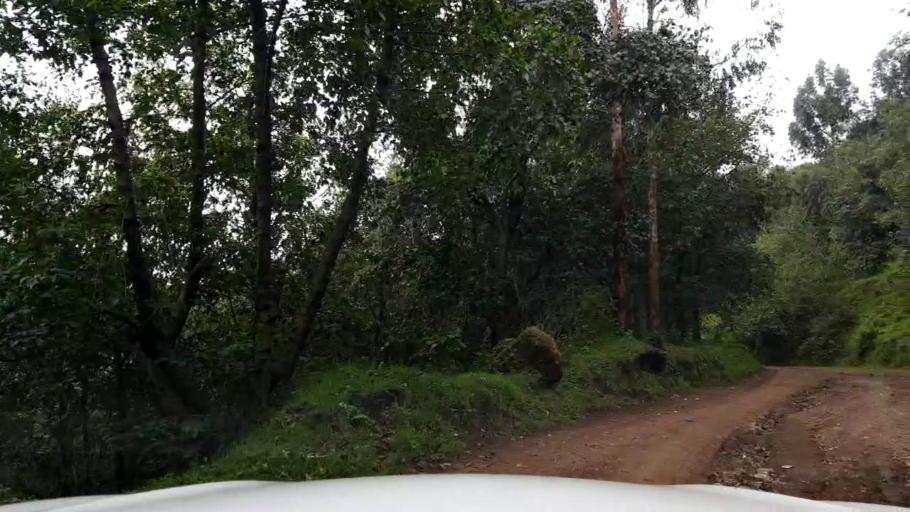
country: RW
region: Western Province
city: Gisenyi
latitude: -1.6559
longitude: 29.4176
